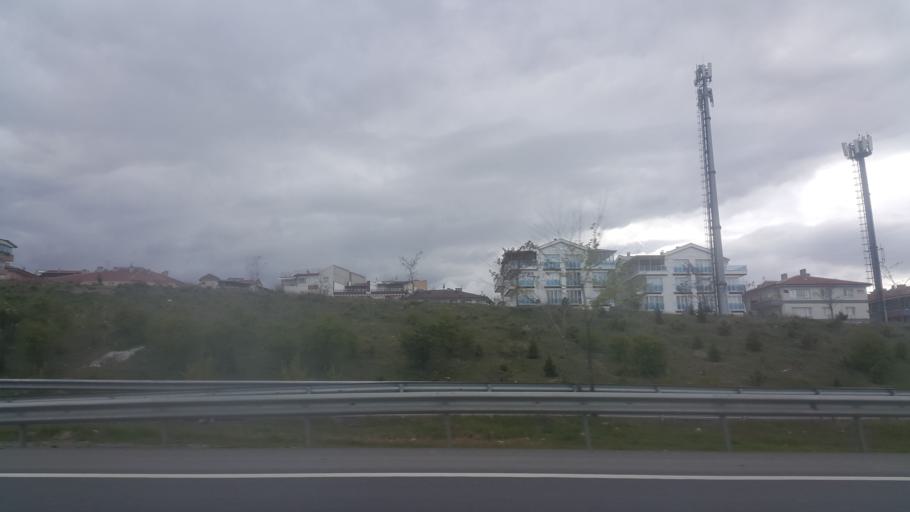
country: TR
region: Ankara
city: Etimesgut
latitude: 39.9496
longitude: 32.6230
